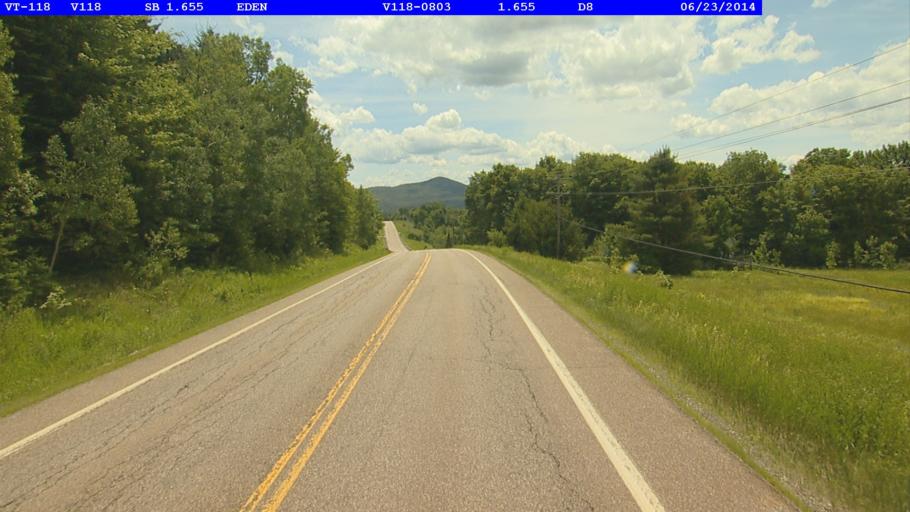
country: US
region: Vermont
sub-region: Lamoille County
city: Hyde Park
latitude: 44.7280
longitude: -72.5620
